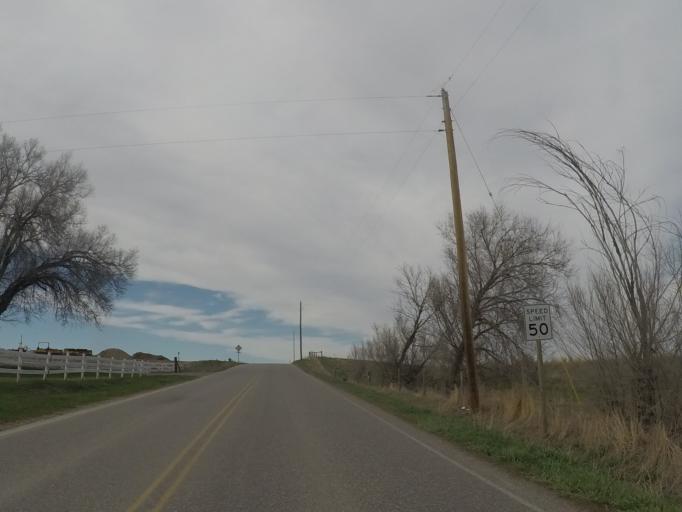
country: US
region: Montana
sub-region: Yellowstone County
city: Laurel
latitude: 45.7120
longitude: -108.6587
